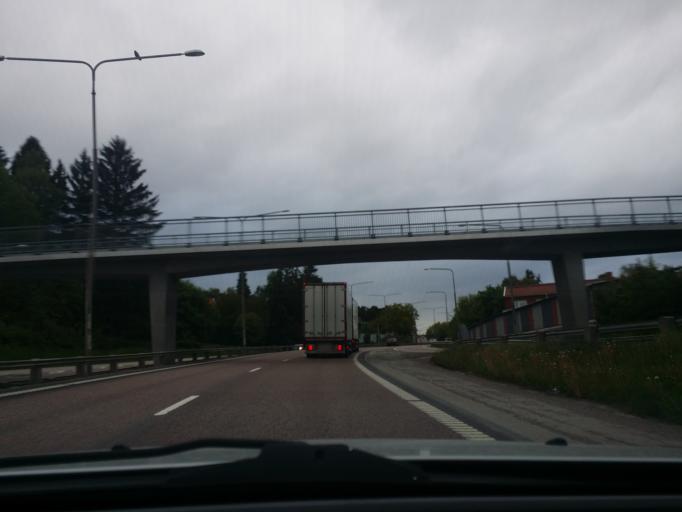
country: SE
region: Vaestmanland
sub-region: Vasteras
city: Vasteras
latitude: 59.6200
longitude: 16.5544
